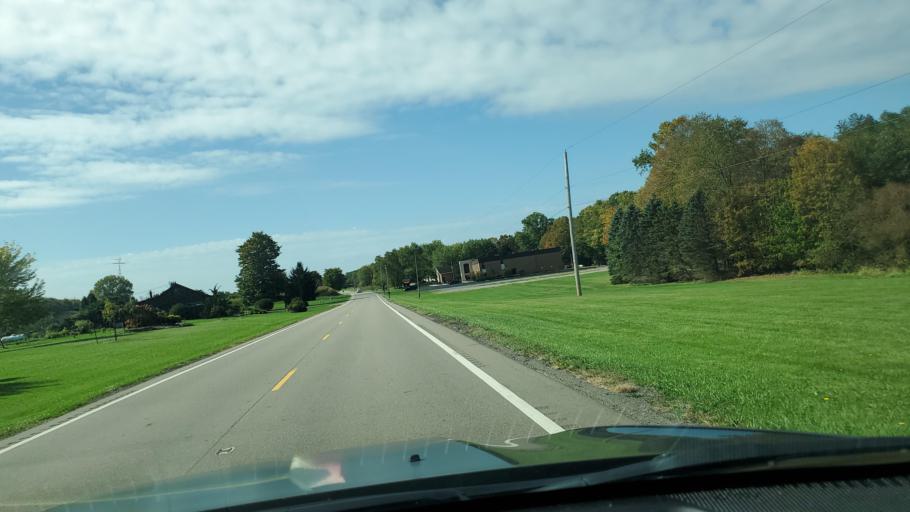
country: US
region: Ohio
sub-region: Trumbull County
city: Cortland
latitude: 41.4050
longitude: -80.6136
